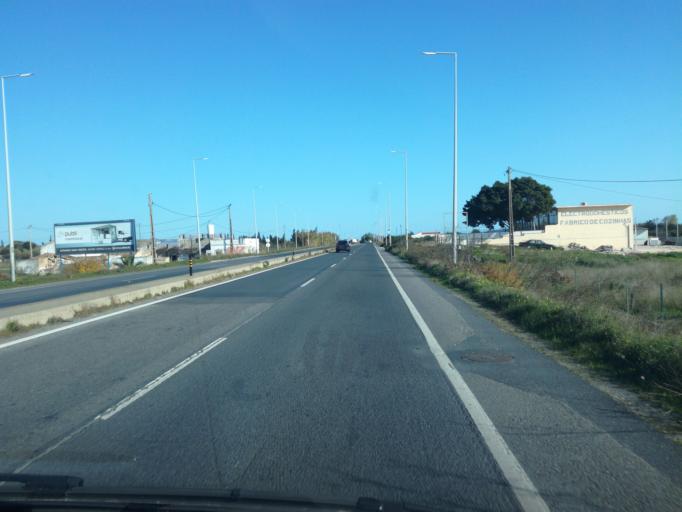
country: PT
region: Faro
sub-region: Faro
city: Faro
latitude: 37.0258
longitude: -7.8903
